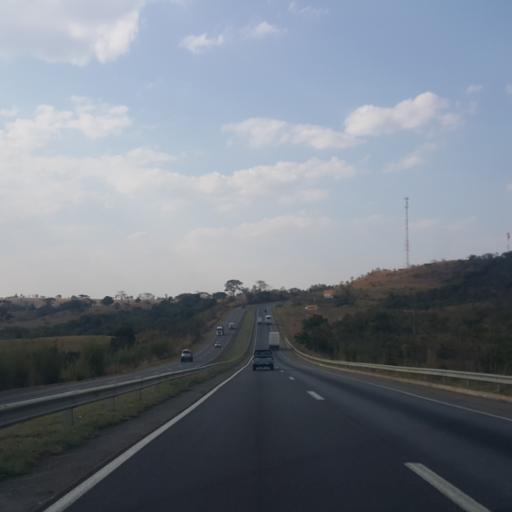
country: BR
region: Goias
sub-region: Abadiania
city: Abadiania
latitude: -16.1042
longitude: -48.5241
